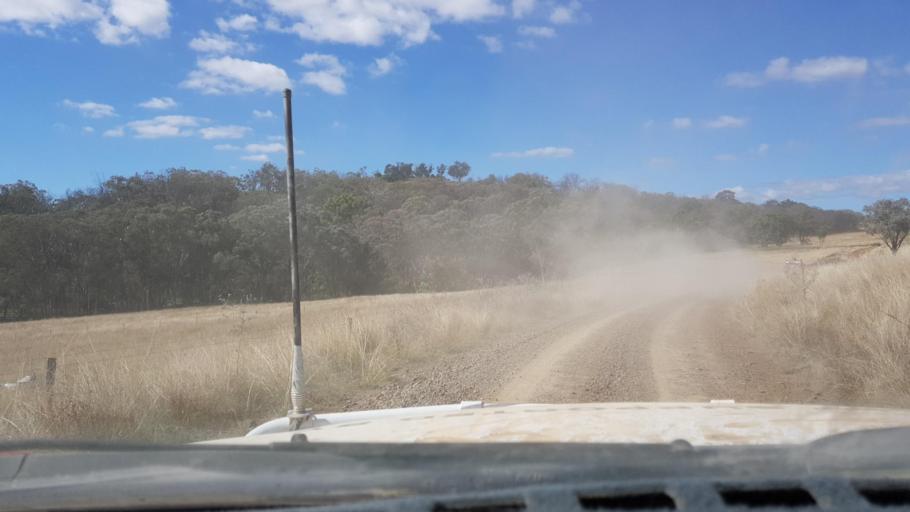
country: AU
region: New South Wales
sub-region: Tamworth Municipality
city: Manilla
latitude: -30.4303
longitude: 150.8212
